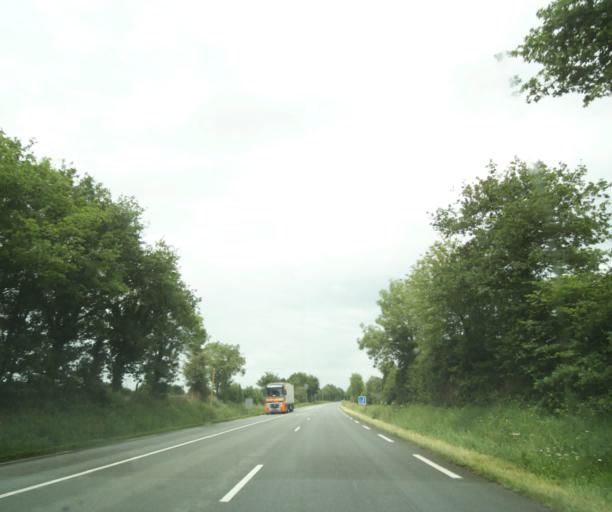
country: FR
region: Poitou-Charentes
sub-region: Departement des Deux-Sevres
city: Le Tallud
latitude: 46.6208
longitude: -0.2814
